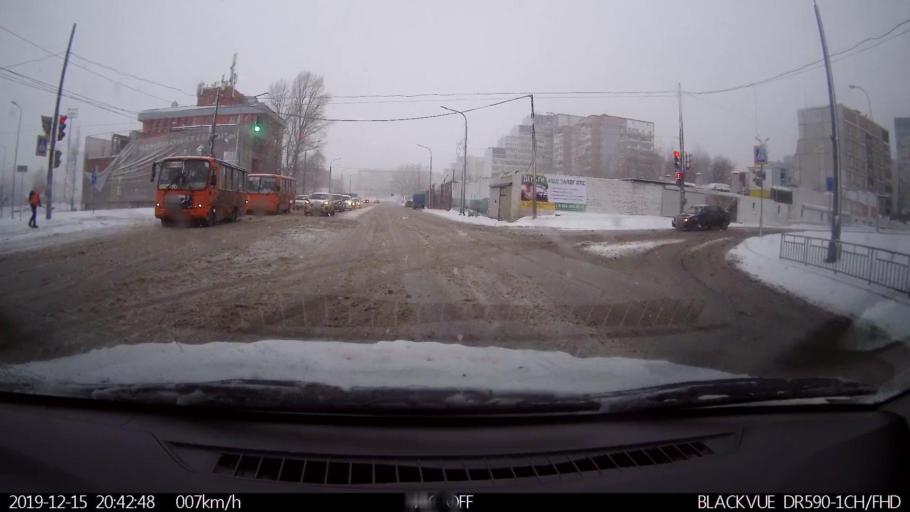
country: RU
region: Nizjnij Novgorod
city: Nizhniy Novgorod
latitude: 56.3399
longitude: 43.9440
